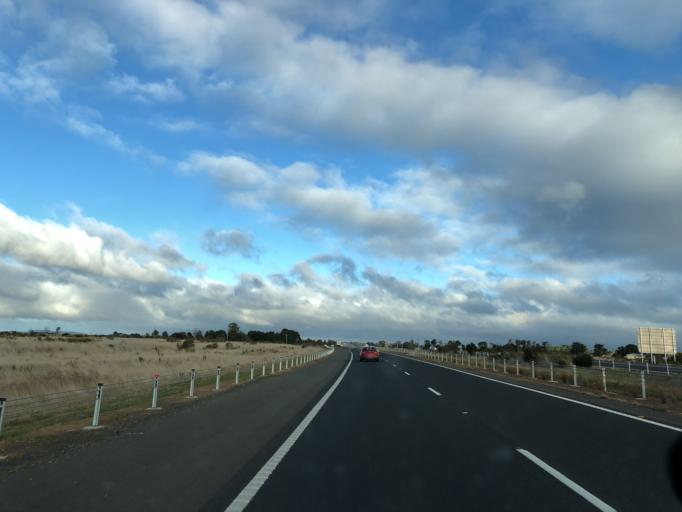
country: AU
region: Victoria
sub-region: Mount Alexander
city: Castlemaine
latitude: -37.2027
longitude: 144.4076
